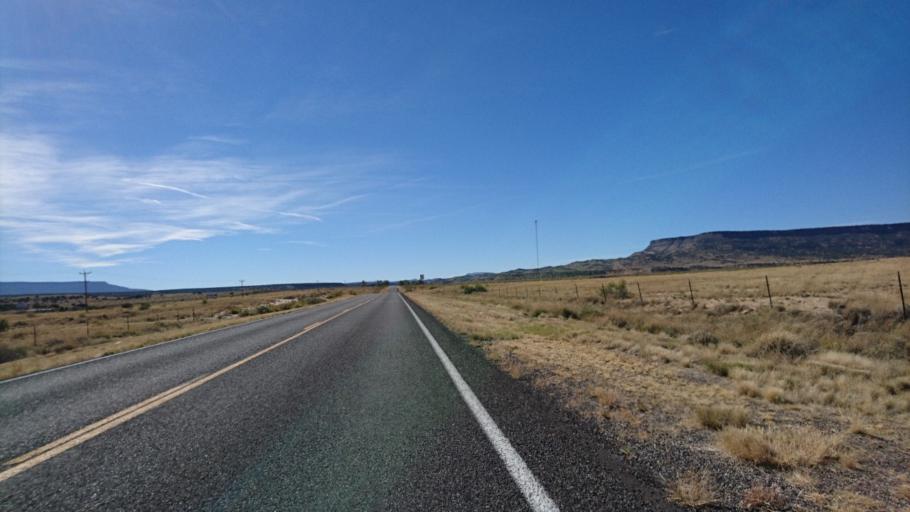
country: US
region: New Mexico
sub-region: Cibola County
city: Skyline-Ganipa
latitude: 35.0804
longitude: -107.6362
